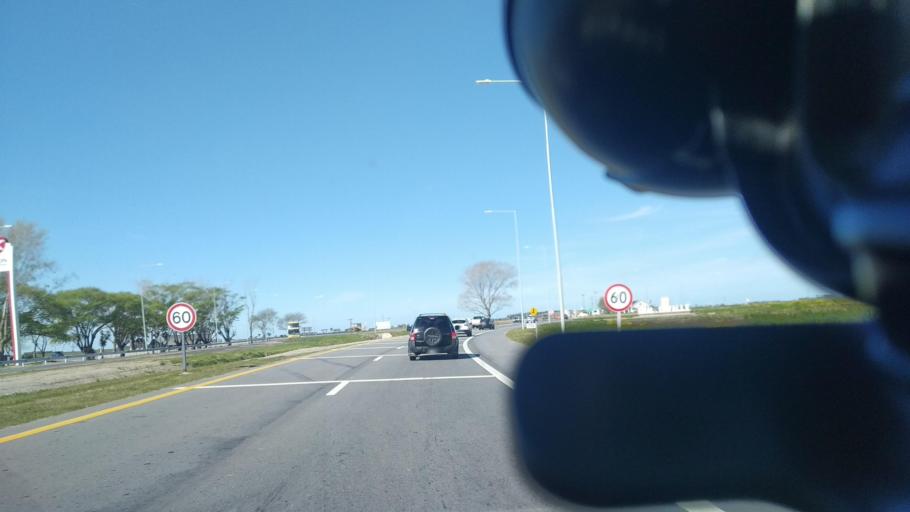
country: AR
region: Buenos Aires
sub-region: Partido de General Lavalle
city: General Lavalle
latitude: -36.4311
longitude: -56.9176
